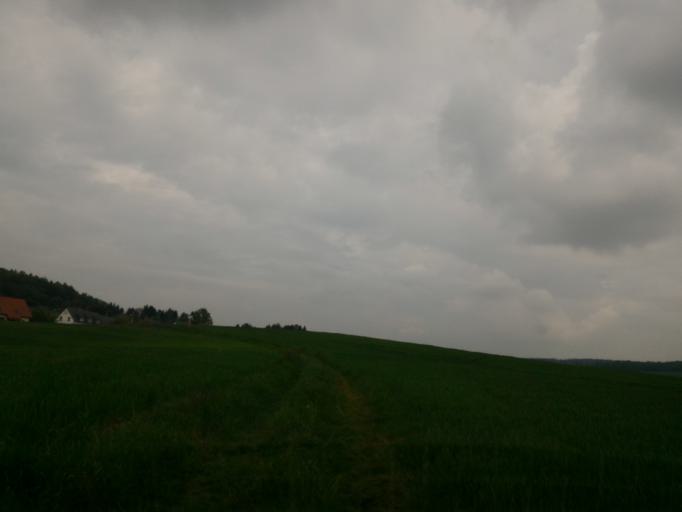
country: DE
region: Saxony
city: Grossschonau
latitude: 50.8989
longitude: 14.6743
